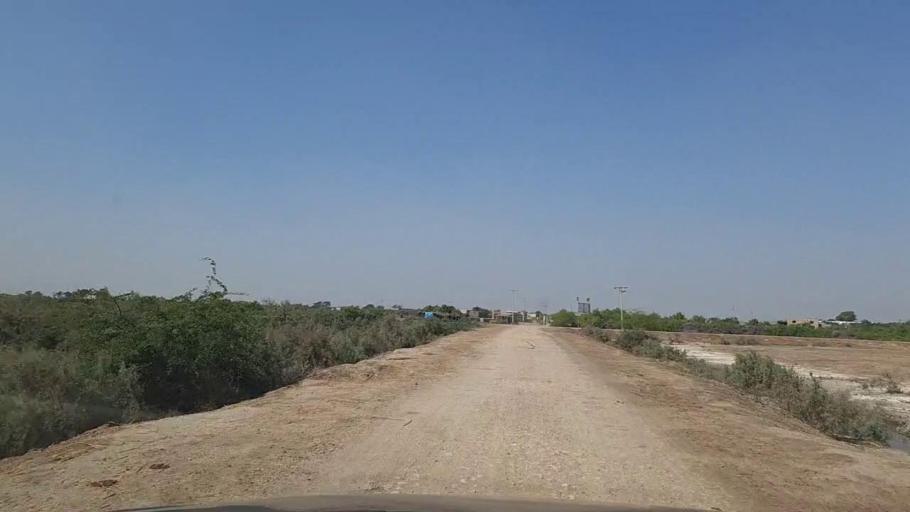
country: PK
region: Sindh
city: Daro Mehar
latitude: 24.8365
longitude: 68.1400
